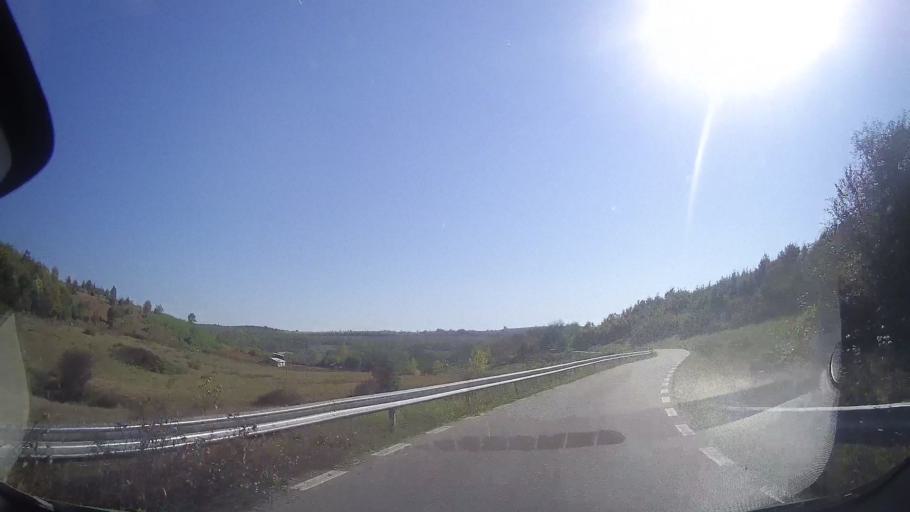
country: RO
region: Timis
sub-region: Comuna Ohaba Lunga
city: Ohaba Lunga
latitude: 45.9079
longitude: 21.9757
